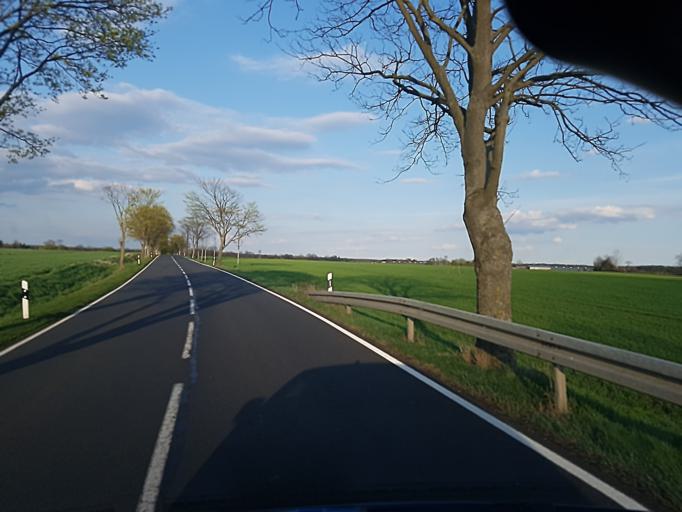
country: DE
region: Saxony
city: Bad Duben
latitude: 51.6222
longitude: 12.5397
